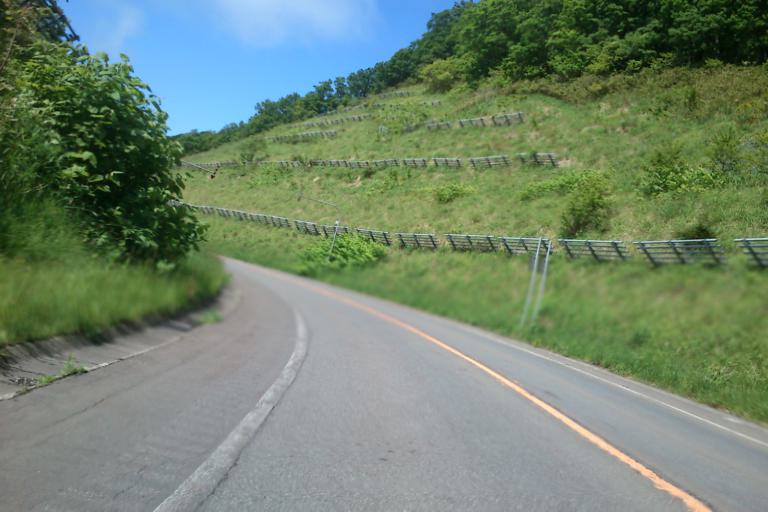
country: JP
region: Hokkaido
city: Ishikari
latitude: 43.4835
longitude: 141.4006
